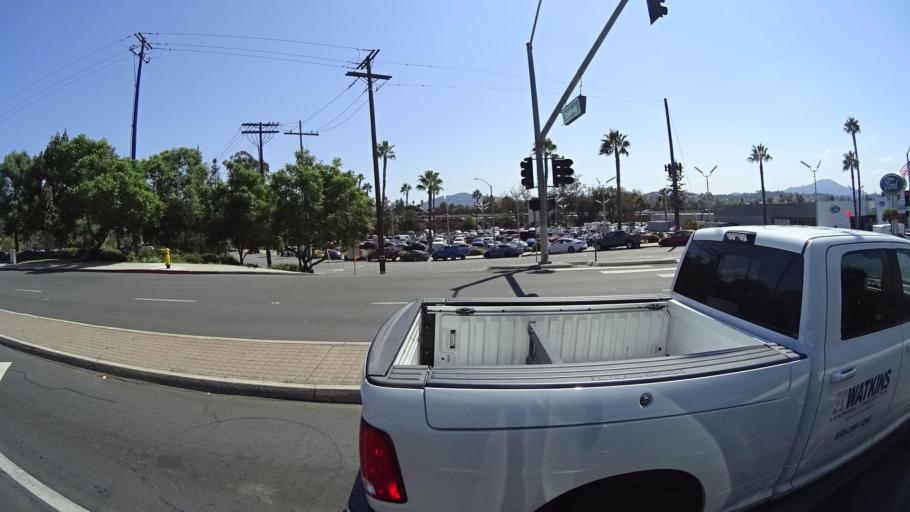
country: US
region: California
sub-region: San Diego County
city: Bostonia
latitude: 32.8080
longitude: -116.9218
